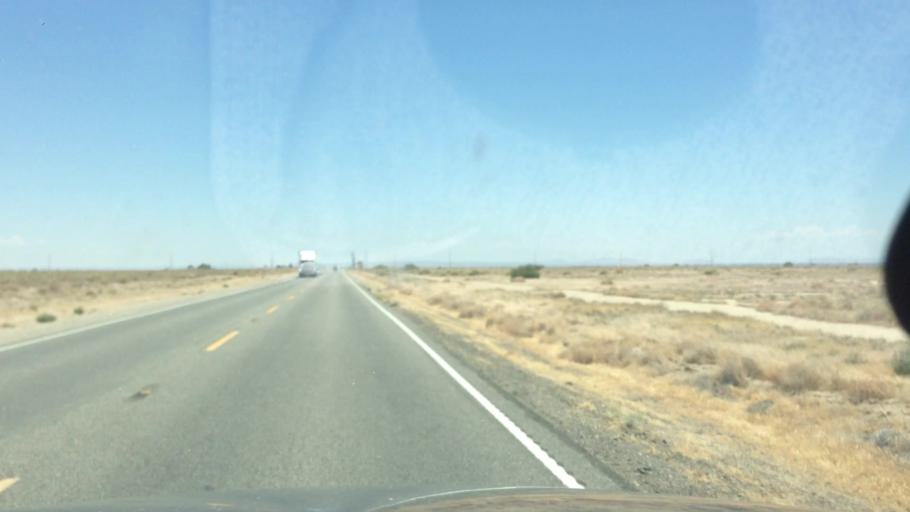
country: US
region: California
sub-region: Kern County
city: Rosamond
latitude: 34.7766
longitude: -118.2451
